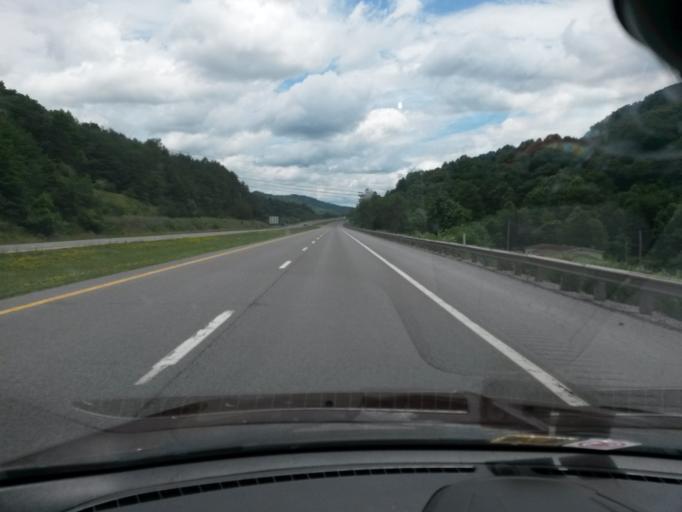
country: US
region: West Virginia
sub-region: Mercer County
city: Athens
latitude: 37.3428
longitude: -80.9910
